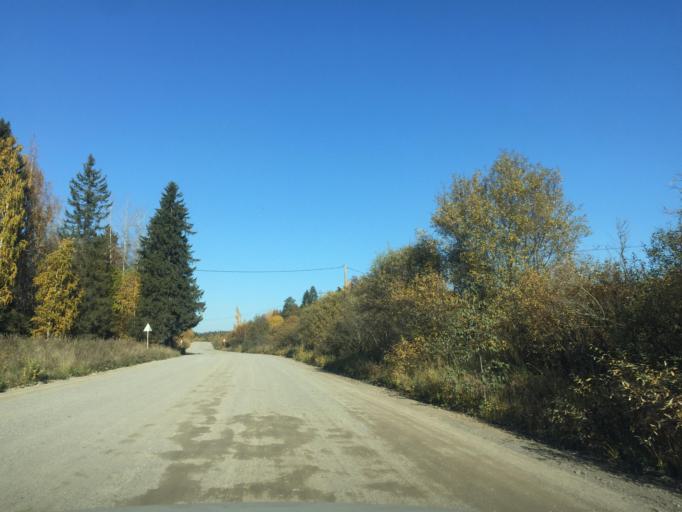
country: RU
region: Leningrad
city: Kuznechnoye
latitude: 61.3130
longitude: 29.9428
